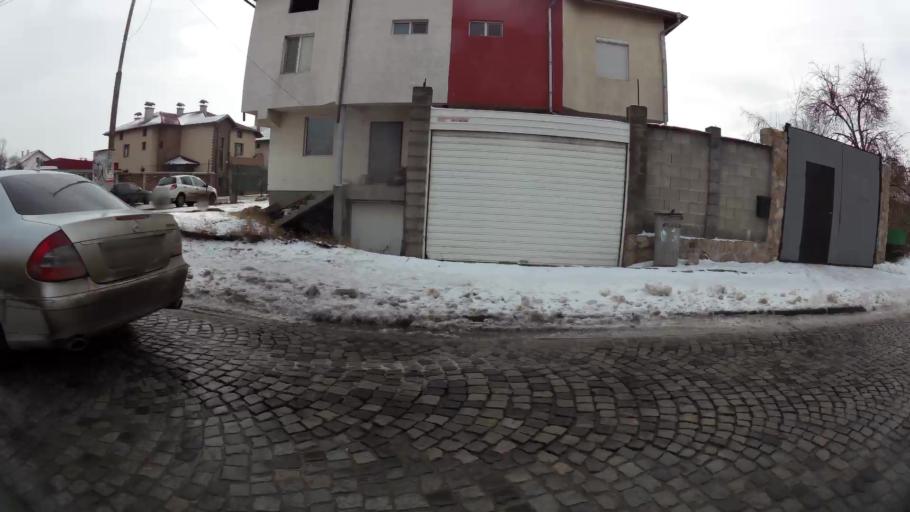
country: BG
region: Sofia-Capital
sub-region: Stolichna Obshtina
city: Sofia
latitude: 42.7133
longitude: 23.4143
